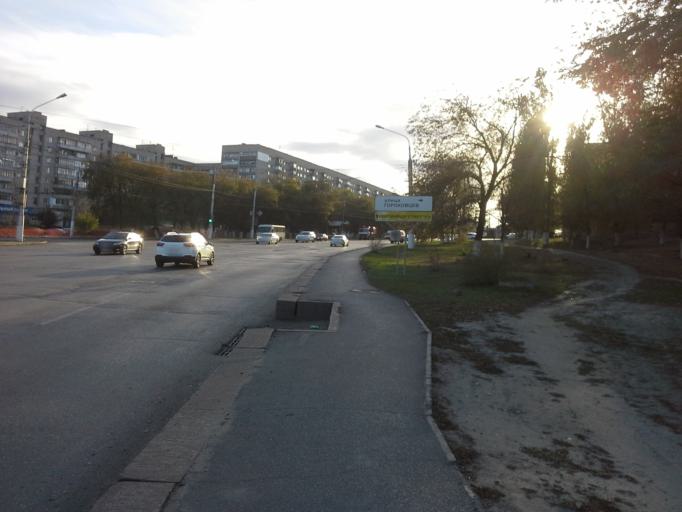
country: RU
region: Volgograd
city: Vodstroy
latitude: 48.8242
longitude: 44.6414
